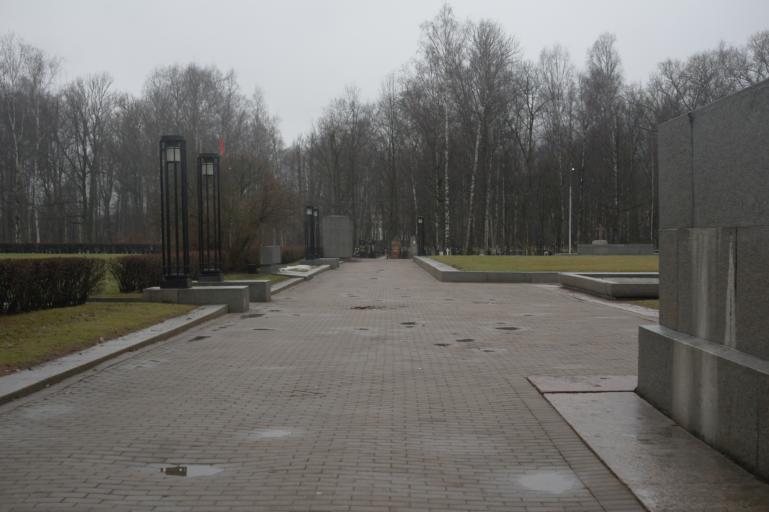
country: RU
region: St.-Petersburg
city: Novaya Derevnya
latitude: 59.9887
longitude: 30.2711
